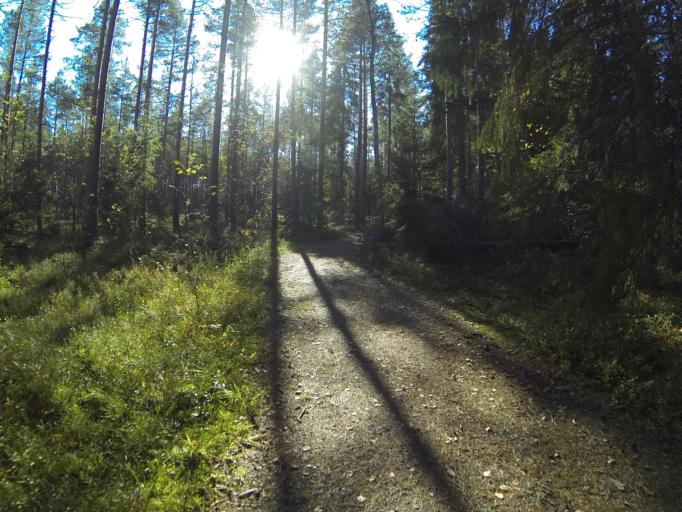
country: FI
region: Varsinais-Suomi
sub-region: Salo
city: Saerkisalo
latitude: 60.1990
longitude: 22.9322
